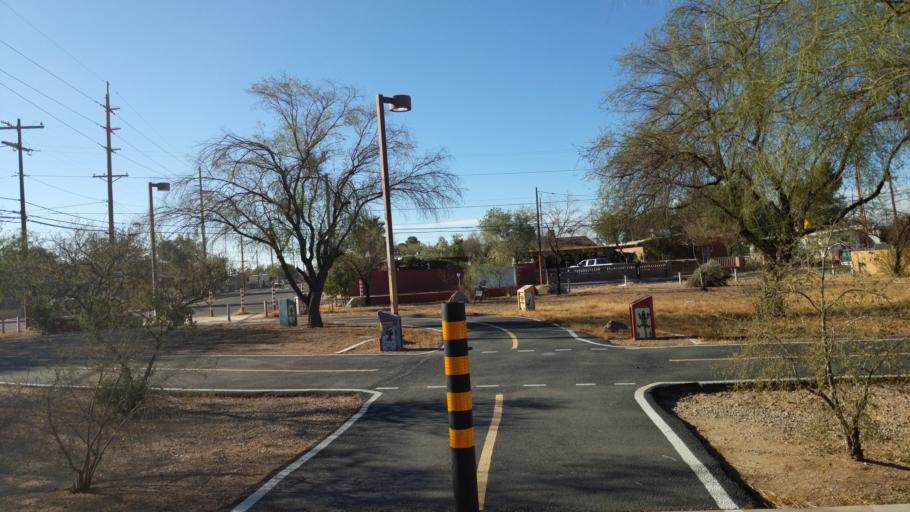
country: US
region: Arizona
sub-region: Pima County
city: South Tucson
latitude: 32.1890
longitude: -110.9761
